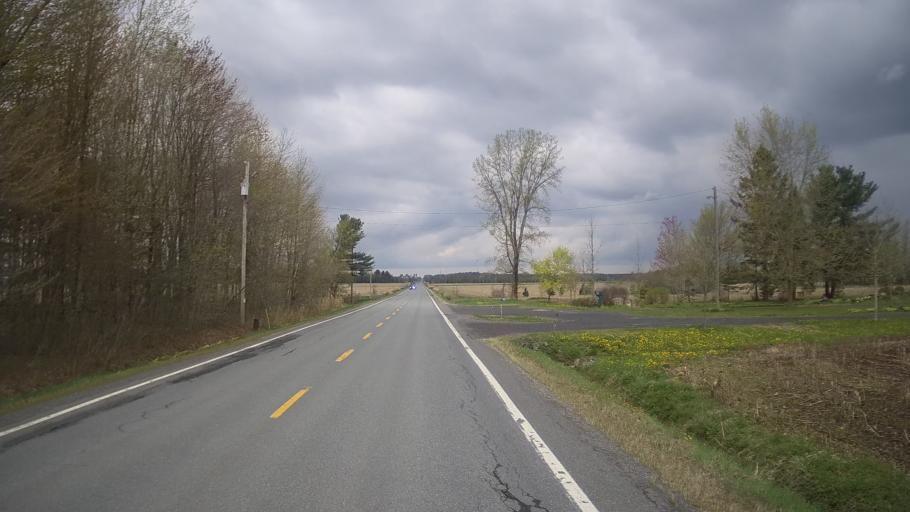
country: CA
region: Quebec
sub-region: Monteregie
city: Farnham
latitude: 45.2509
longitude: -72.9015
